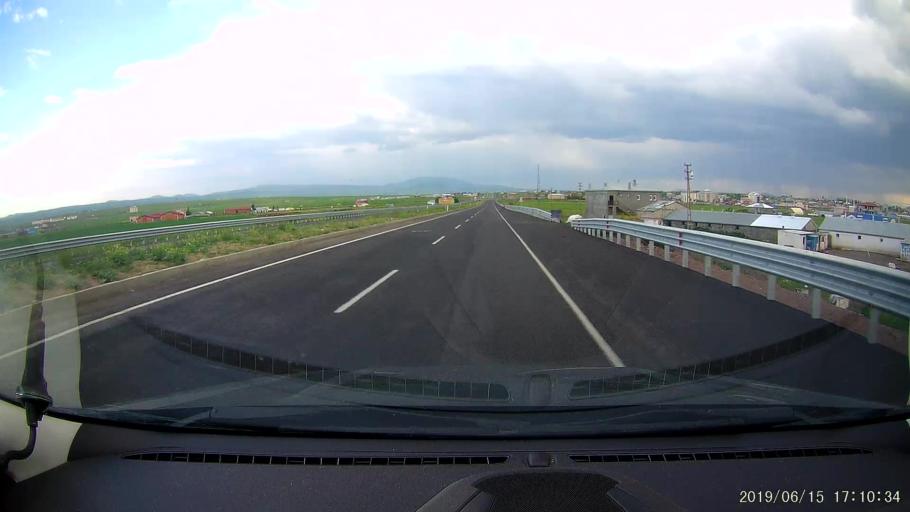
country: TR
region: Kars
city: Kars
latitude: 40.6207
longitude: 43.1337
